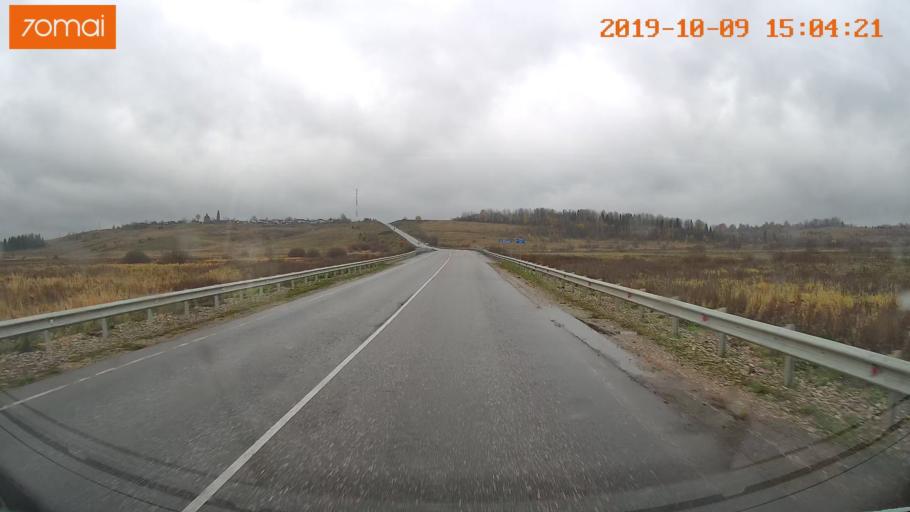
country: RU
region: Kostroma
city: Chistyye Bory
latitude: 58.2595
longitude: 41.6679
